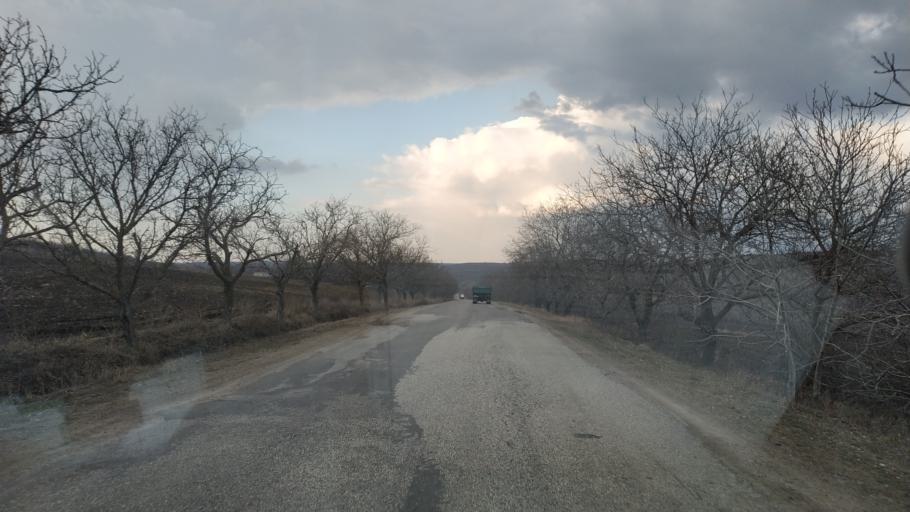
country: MD
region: Anenii Noi
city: Anenii Noi
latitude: 46.9341
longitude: 29.2861
